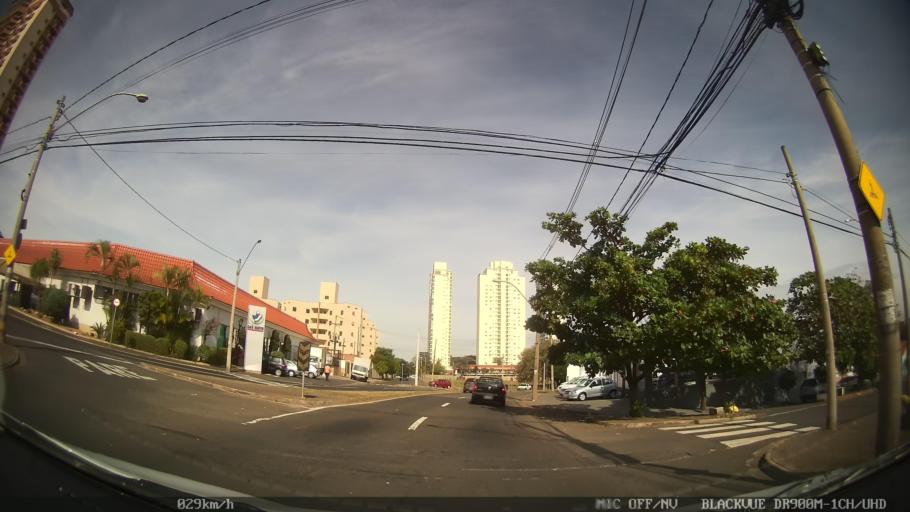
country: BR
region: Sao Paulo
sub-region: Piracicaba
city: Piracicaba
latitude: -22.7153
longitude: -47.6580
